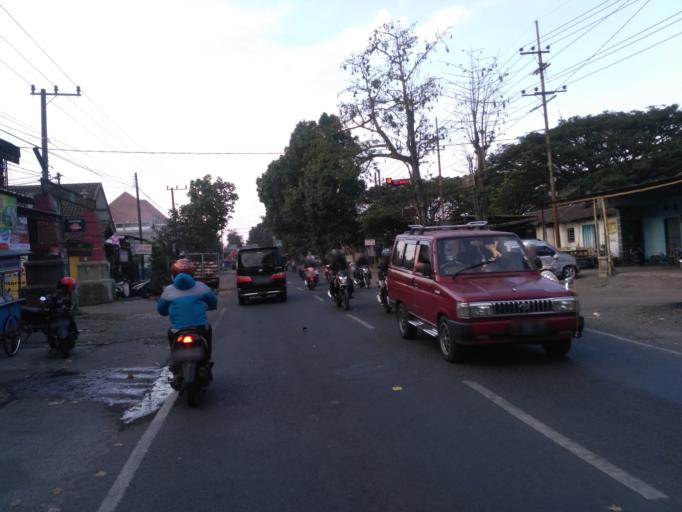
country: ID
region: East Java
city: Kebonsari
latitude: -8.0304
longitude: 112.6148
